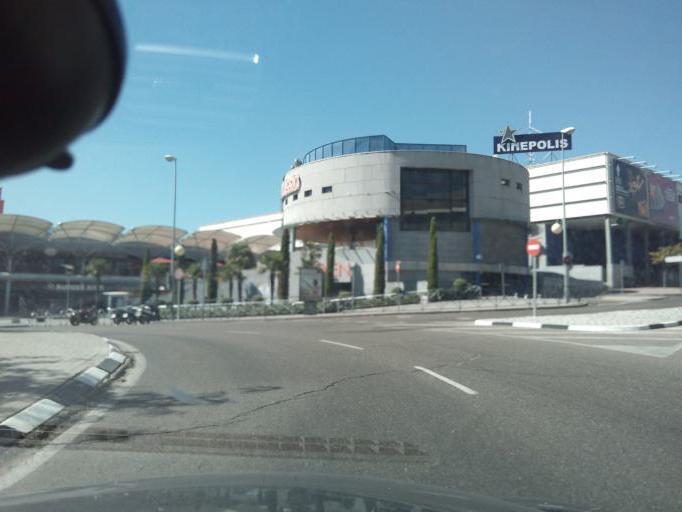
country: ES
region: Madrid
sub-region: Provincia de Madrid
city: Alcobendas
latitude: 40.5312
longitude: -3.6390
